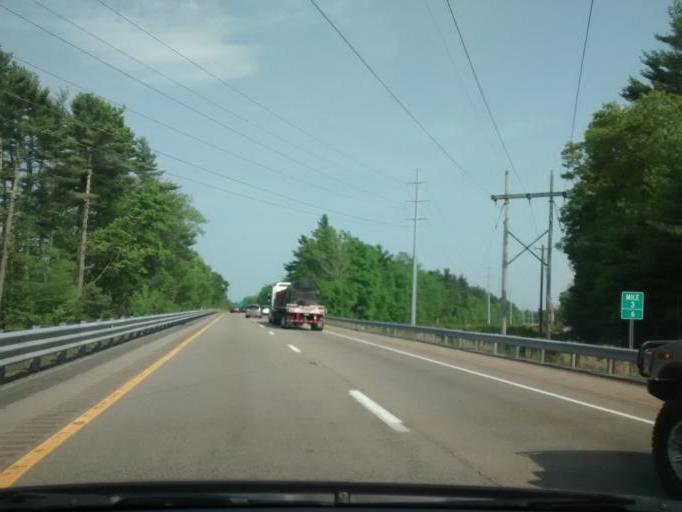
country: US
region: Massachusetts
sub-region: Plymouth County
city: West Wareham
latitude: 41.8122
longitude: -70.7898
